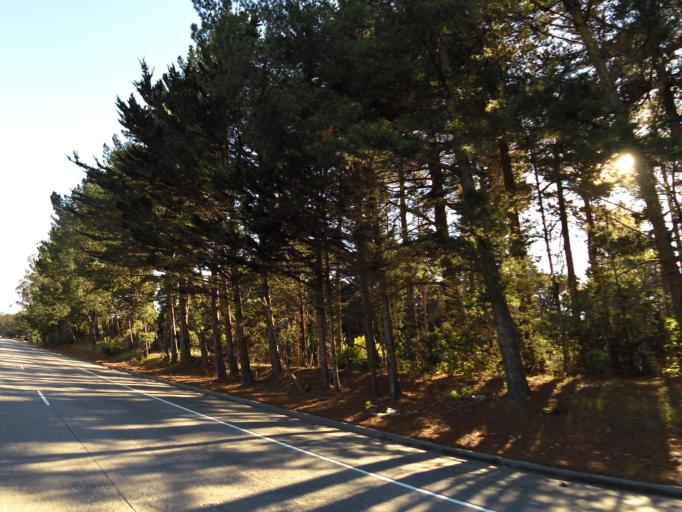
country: US
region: California
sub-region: San Mateo County
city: Millbrae
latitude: 37.5912
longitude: -122.4146
